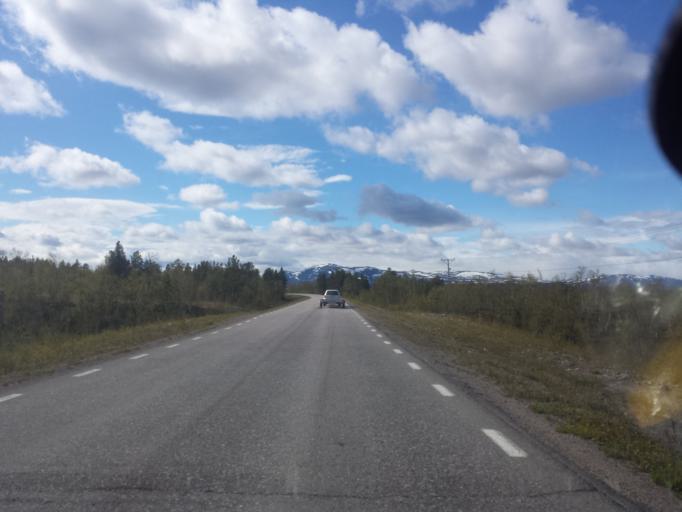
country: SE
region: Norrbotten
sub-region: Kiruna Kommun
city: Kiruna
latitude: 67.9933
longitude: 19.9103
